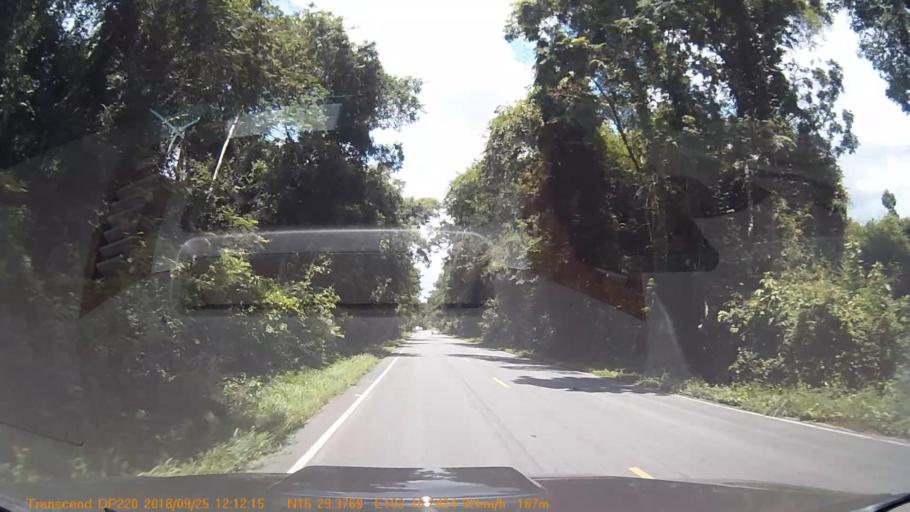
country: TH
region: Kalasin
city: Huai Mek
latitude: 16.4898
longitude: 103.2707
